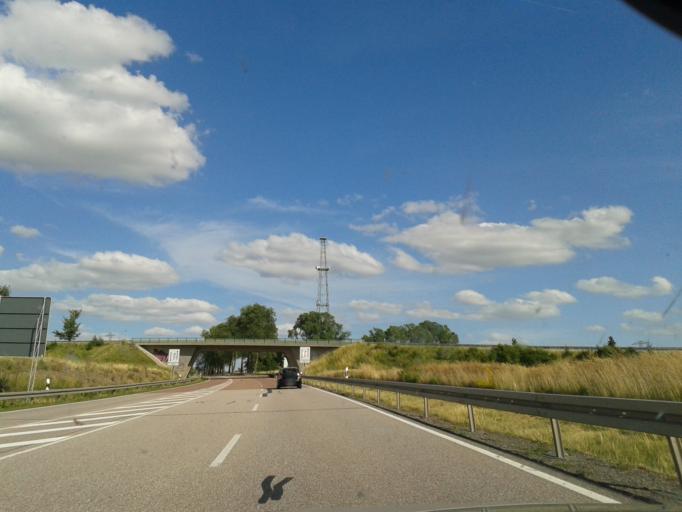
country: DE
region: Saxony-Anhalt
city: Klostermansfeld
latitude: 51.5867
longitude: 11.5096
